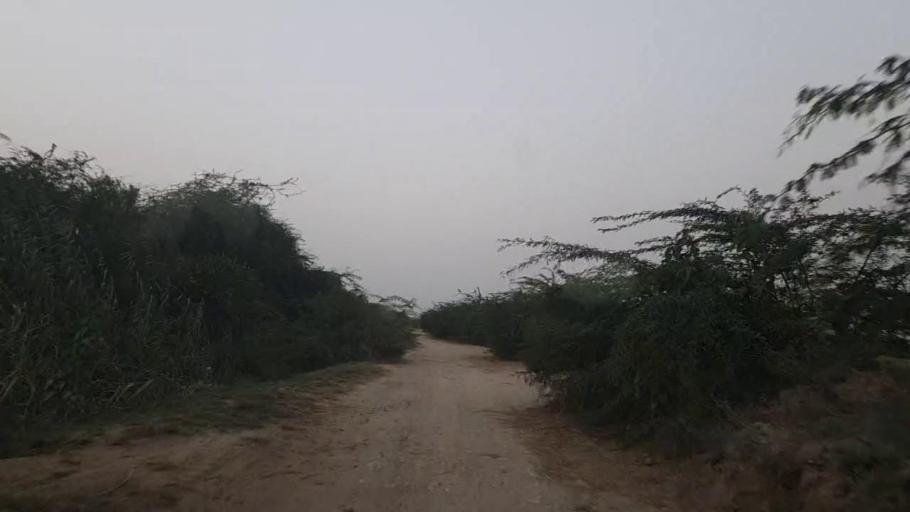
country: PK
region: Sindh
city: Mirpur Sakro
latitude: 24.5766
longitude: 67.7865
